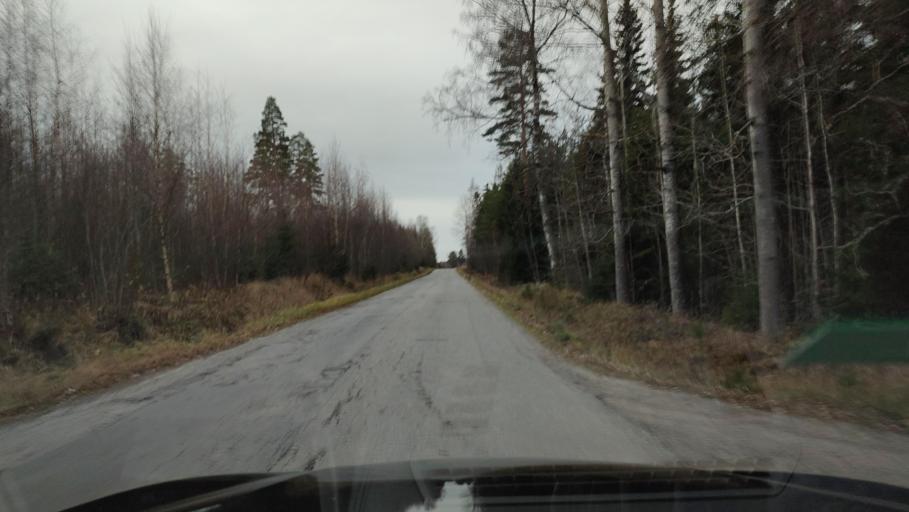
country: FI
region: Ostrobothnia
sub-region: Sydosterbotten
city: Naerpes
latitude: 62.4249
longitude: 21.4136
